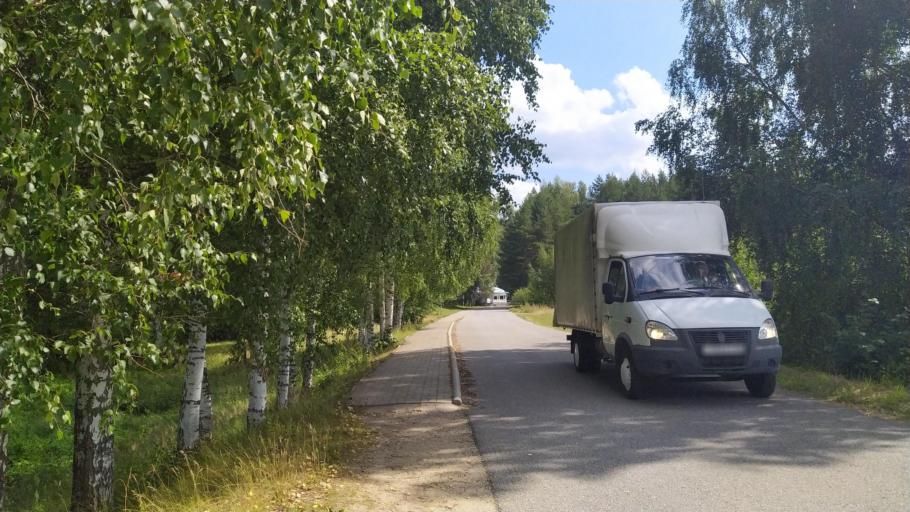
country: RU
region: Pskov
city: Pushkinskiye Gory
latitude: 57.0768
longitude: 28.9540
